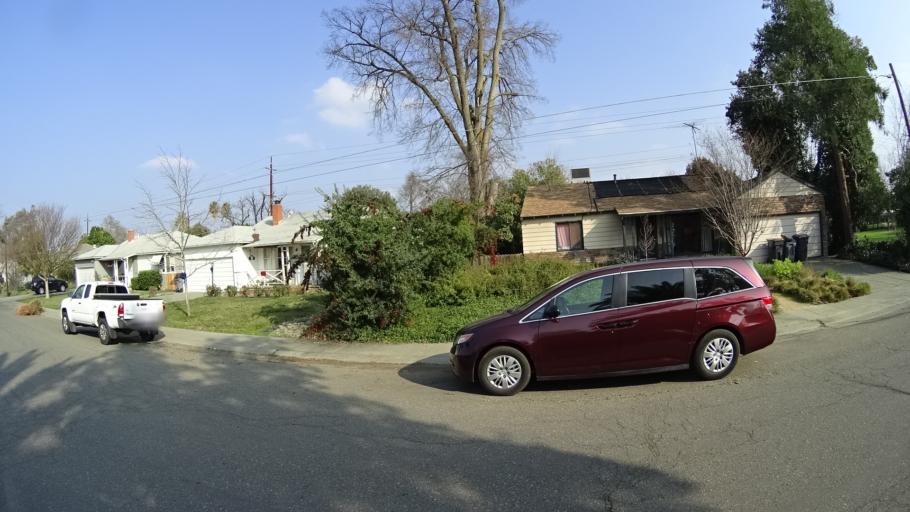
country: US
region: California
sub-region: Yolo County
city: Davis
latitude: 38.5510
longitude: -121.7365
